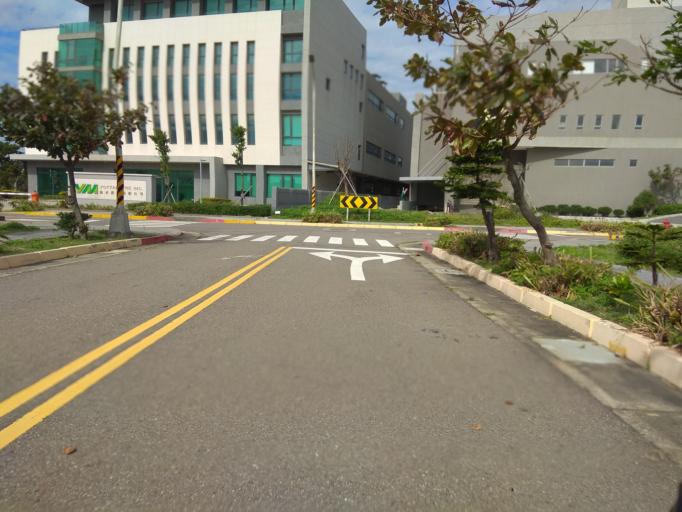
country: TW
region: Taiwan
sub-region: Hsinchu
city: Zhubei
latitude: 25.0375
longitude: 121.0697
